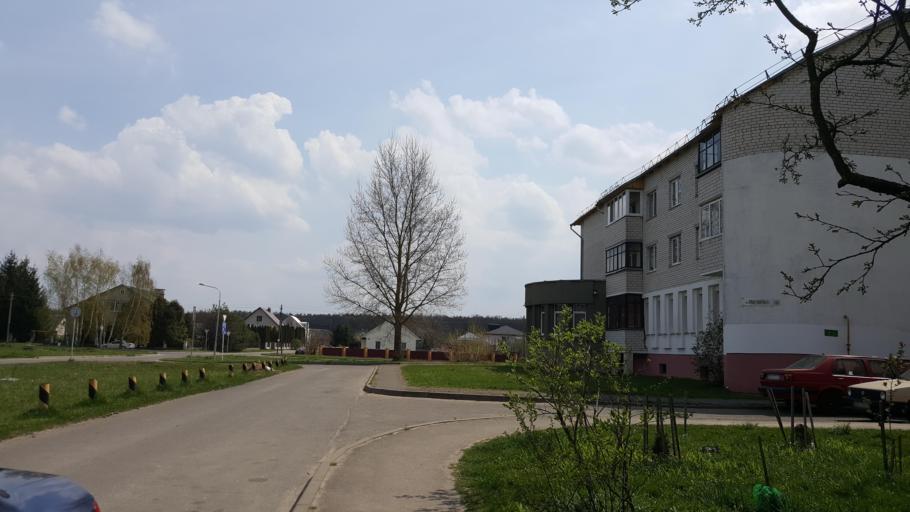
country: BY
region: Brest
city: Zhabinka
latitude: 52.1922
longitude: 24.0343
